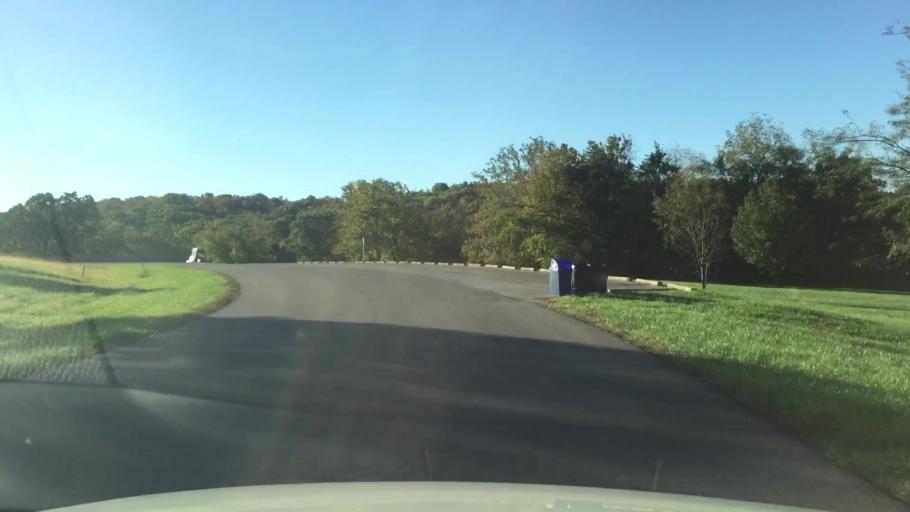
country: US
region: Kansas
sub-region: Johnson County
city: Lenexa
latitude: 38.9845
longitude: -94.7940
